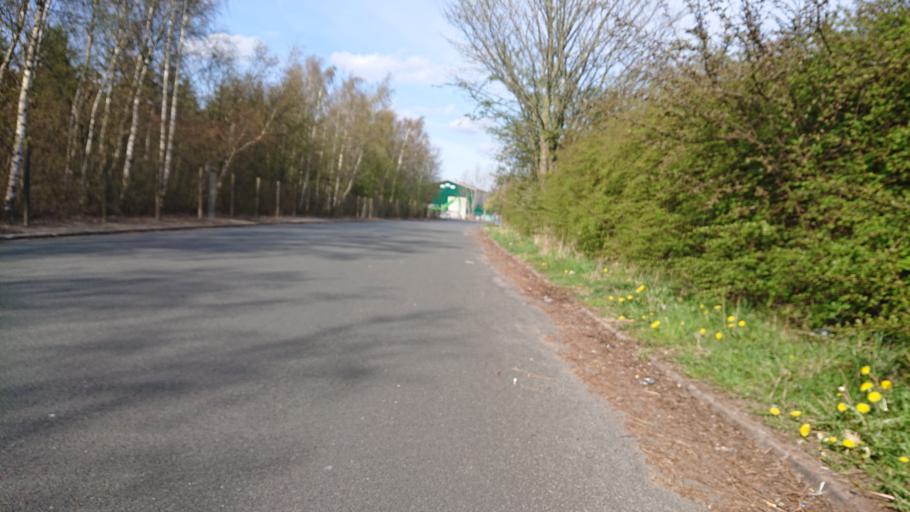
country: DK
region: South Denmark
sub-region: Nyborg Kommune
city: Nyborg
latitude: 55.3111
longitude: 10.7628
